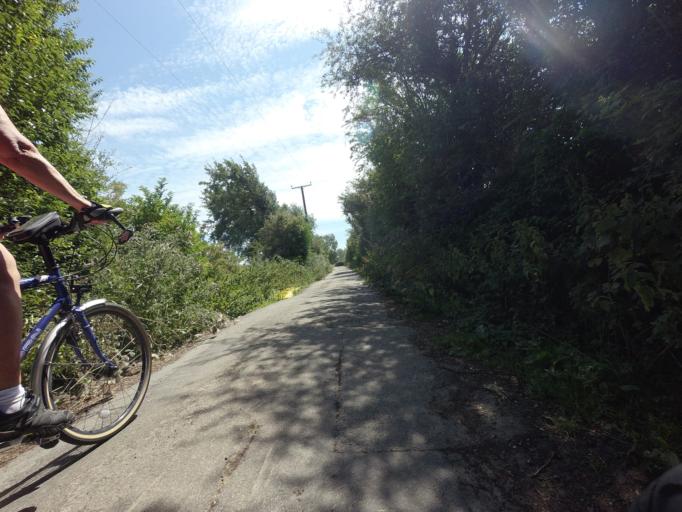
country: GB
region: England
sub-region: Kent
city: Stone
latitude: 50.9908
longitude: 0.8352
